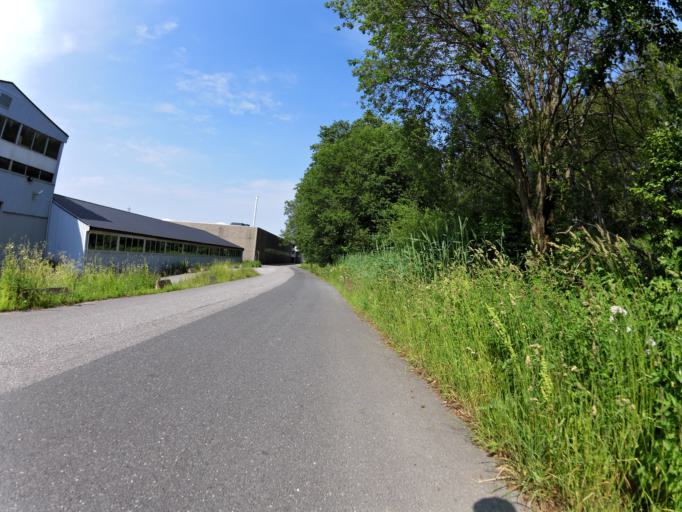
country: NO
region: Ostfold
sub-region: Sarpsborg
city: Sarpsborg
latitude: 59.2700
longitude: 11.1259
